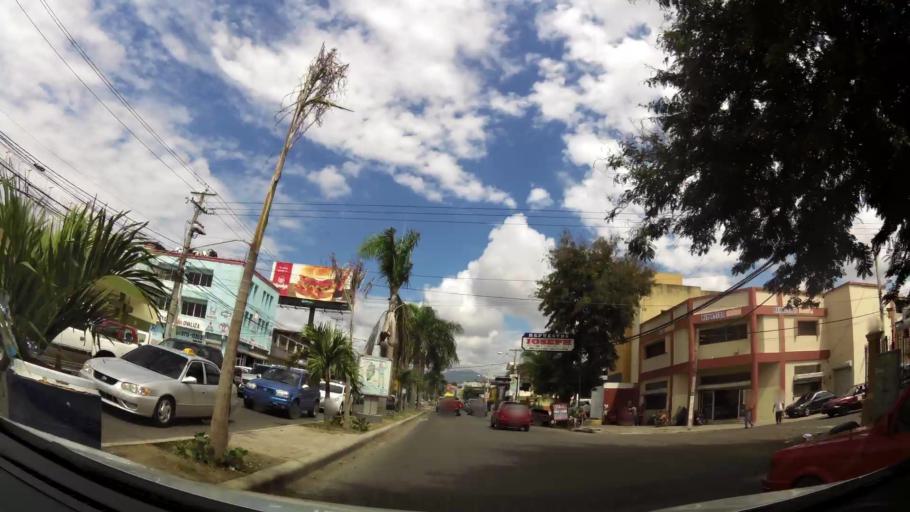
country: DO
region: Santiago
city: Santiago de los Caballeros
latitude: 19.4685
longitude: -70.7125
